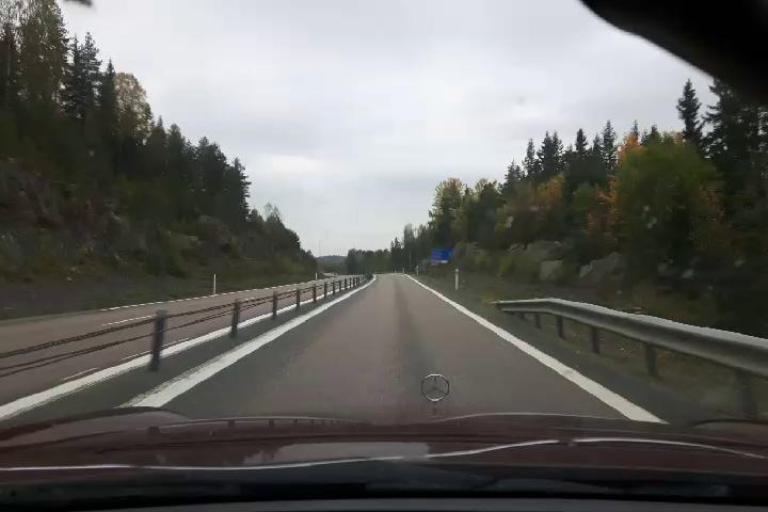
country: SE
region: Vaesternorrland
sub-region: Kramfors Kommun
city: Nordingra
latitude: 62.9354
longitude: 18.0938
